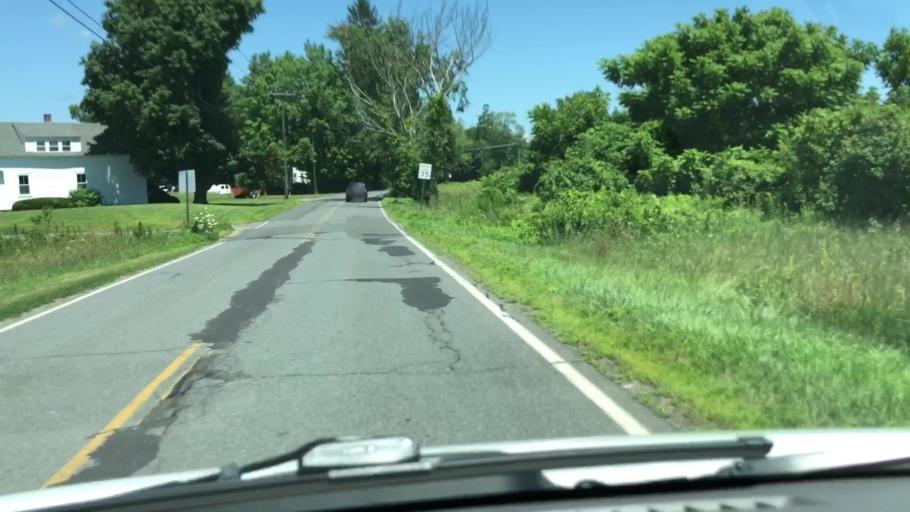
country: US
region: Massachusetts
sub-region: Hampshire County
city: North Amherst
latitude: 42.4062
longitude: -72.5418
